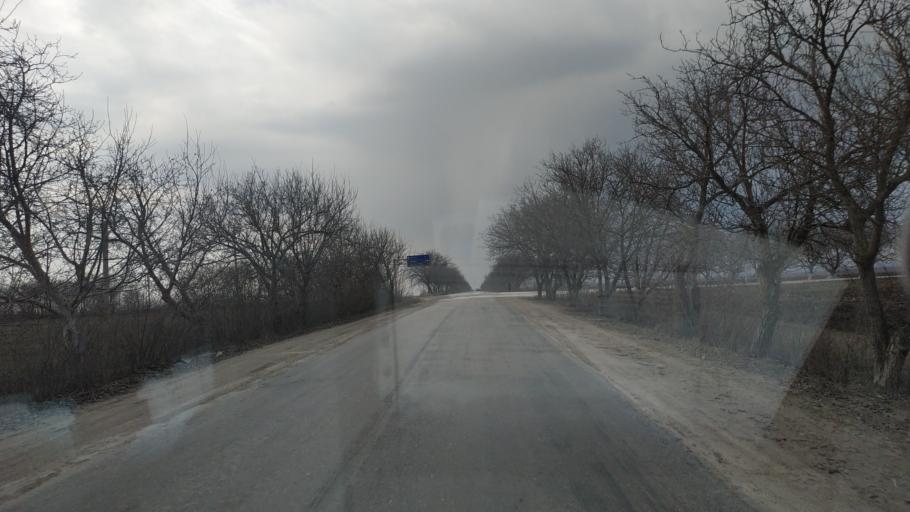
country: MD
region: Telenesti
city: Grigoriopol
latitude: 47.0294
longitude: 29.2918
